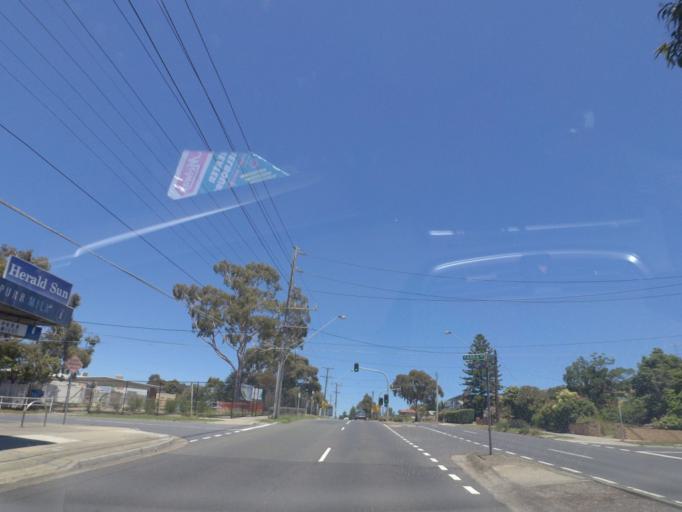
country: AU
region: Victoria
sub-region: Darebin
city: Kingsbury
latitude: -37.7191
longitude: 145.0214
